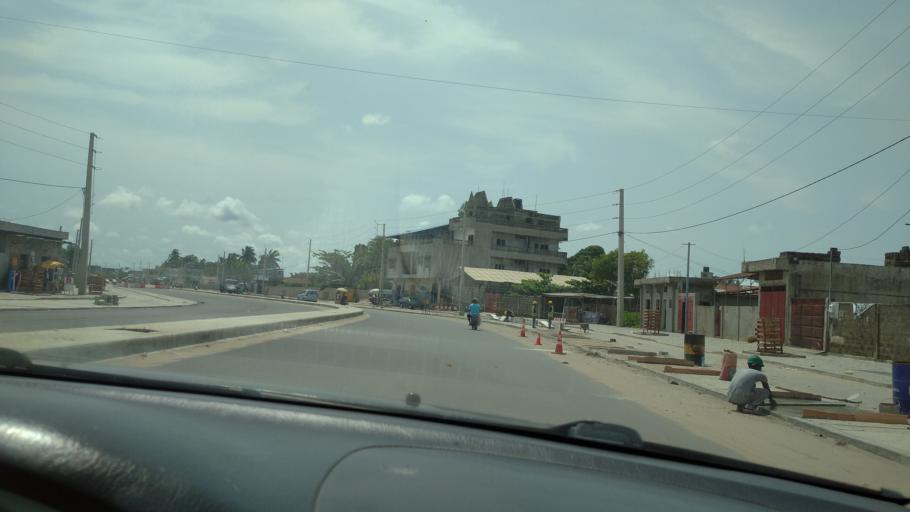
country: BJ
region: Littoral
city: Cotonou
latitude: 6.3740
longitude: 2.4971
